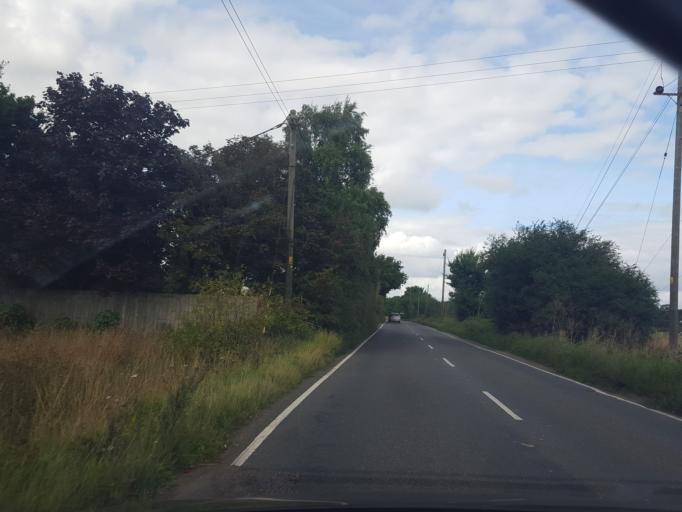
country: GB
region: England
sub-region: Essex
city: Mistley
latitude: 51.9227
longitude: 1.0845
